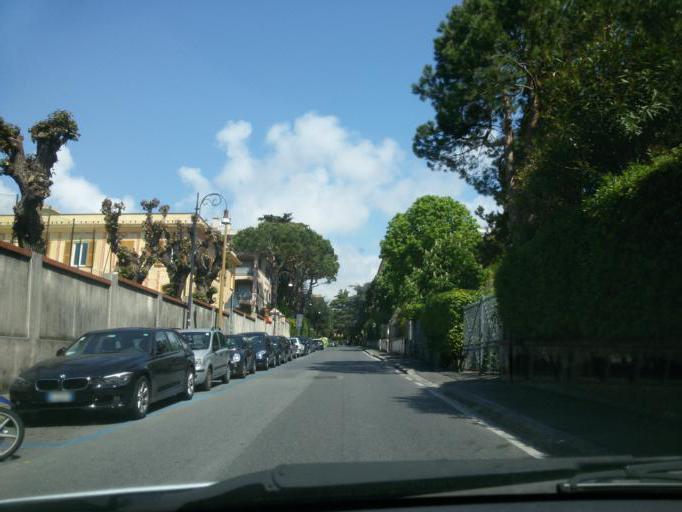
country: IT
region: Liguria
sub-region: Provincia di Genova
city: San Teodoro
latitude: 44.3966
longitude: 8.9586
